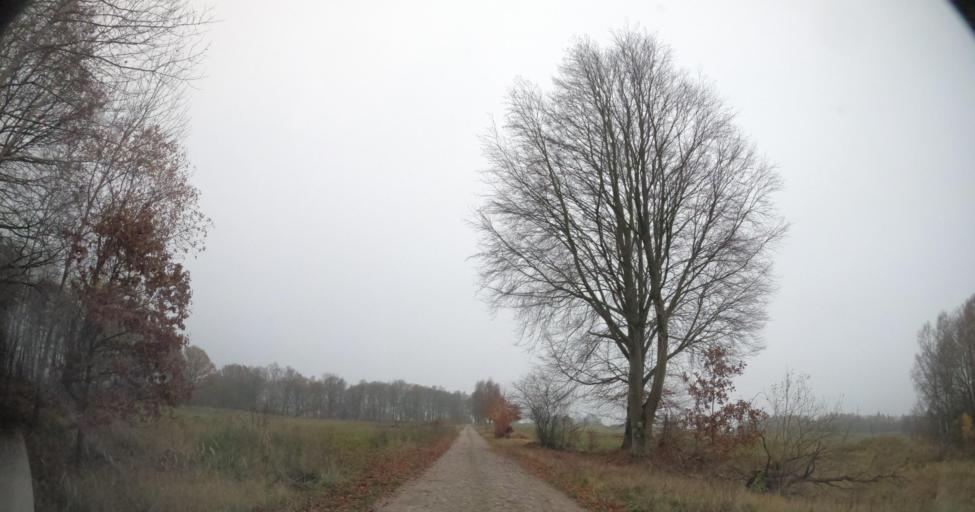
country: PL
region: West Pomeranian Voivodeship
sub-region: Powiat drawski
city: Drawsko Pomorskie
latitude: 53.5461
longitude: 15.7272
